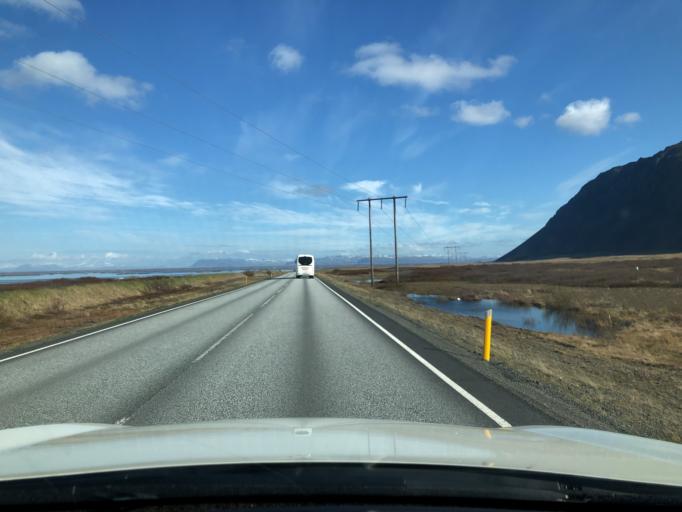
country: IS
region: West
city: Borgarnes
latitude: 64.4543
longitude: -21.9606
